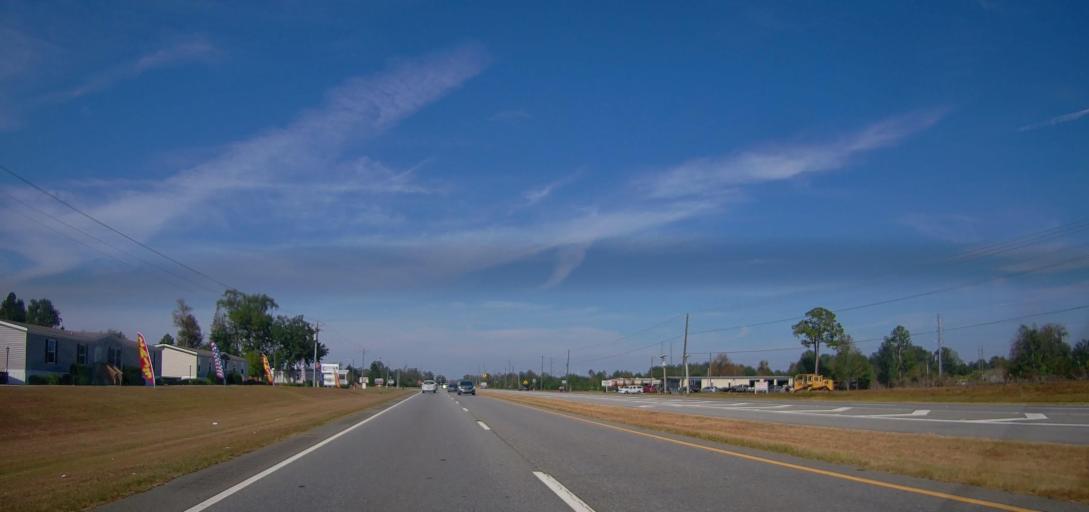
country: US
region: Georgia
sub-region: Dougherty County
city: Putney
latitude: 31.5225
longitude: -84.1157
